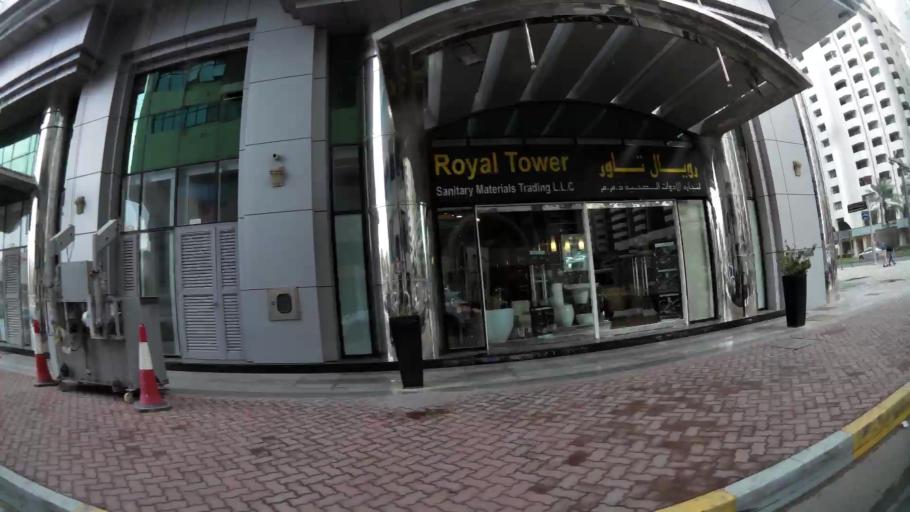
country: AE
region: Abu Dhabi
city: Abu Dhabi
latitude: 24.4870
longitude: 54.3722
